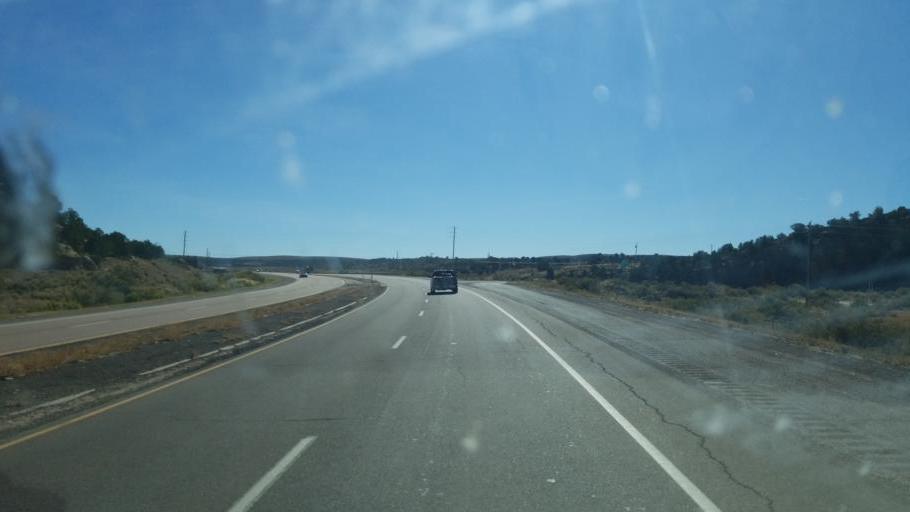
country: US
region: Arizona
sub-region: Apache County
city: Window Rock
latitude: 35.6502
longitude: -109.0378
